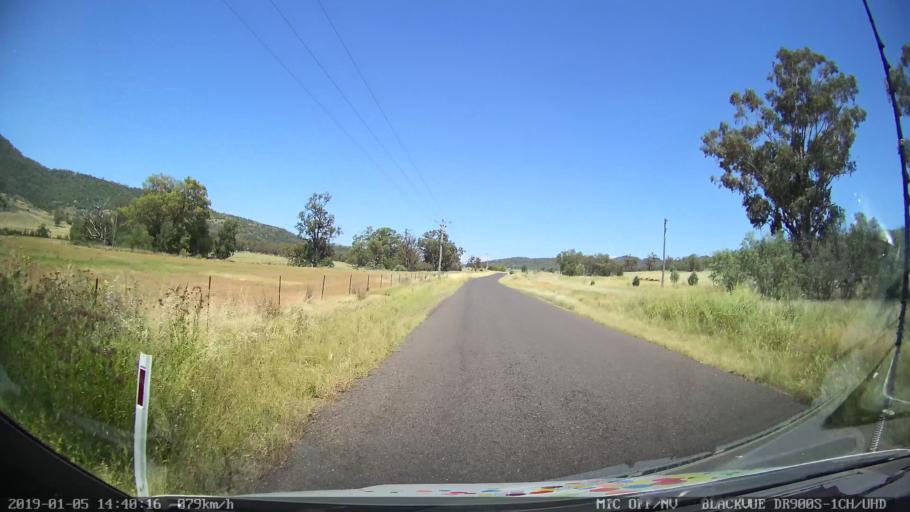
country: AU
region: New South Wales
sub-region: Tamworth Municipality
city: Phillip
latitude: -31.2581
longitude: 150.7106
